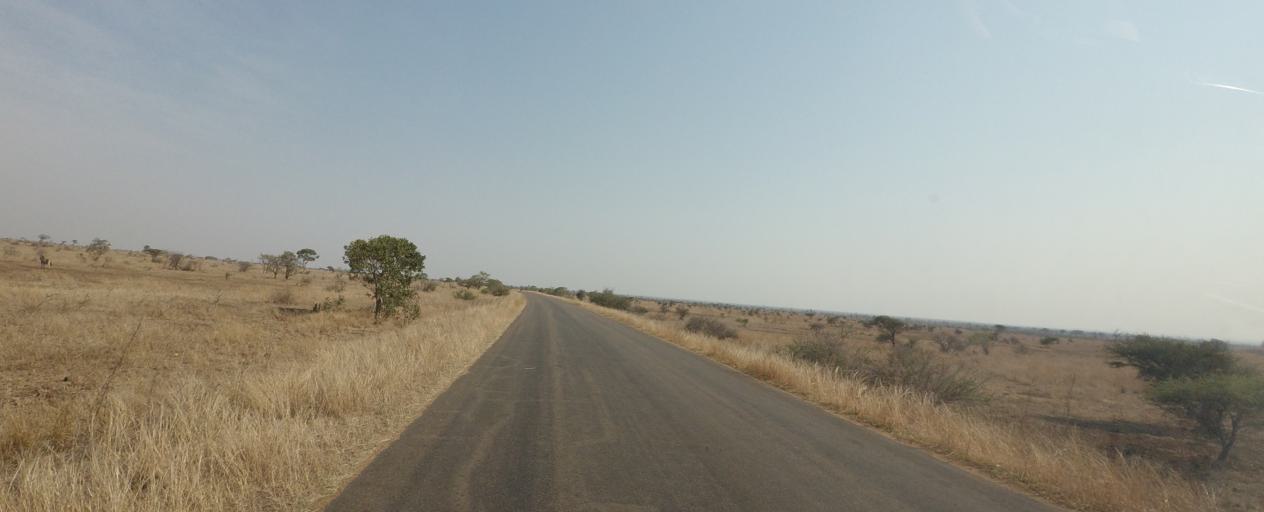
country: ZA
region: Limpopo
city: Thulamahashi
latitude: -24.3277
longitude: 31.7550
